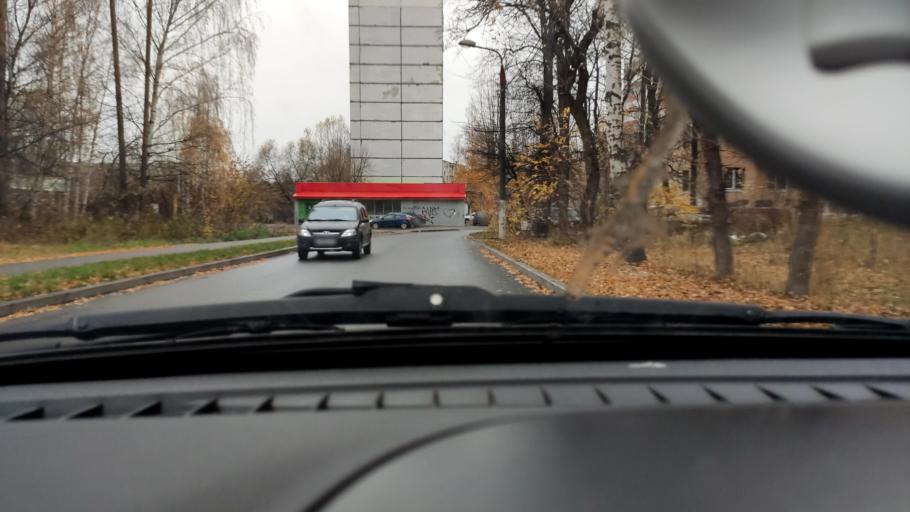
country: RU
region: Perm
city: Kultayevo
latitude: 58.0117
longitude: 55.9666
